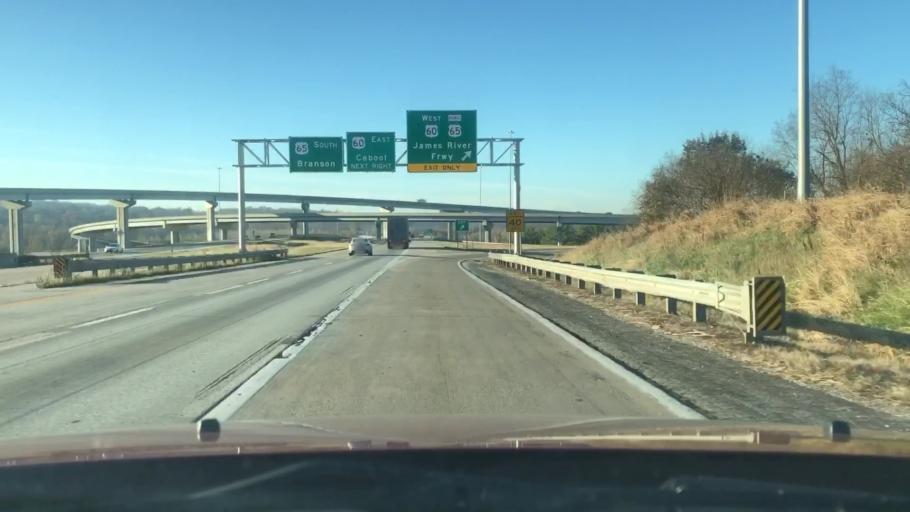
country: US
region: Missouri
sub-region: Greene County
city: Springfield
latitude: 37.1310
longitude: -93.2291
